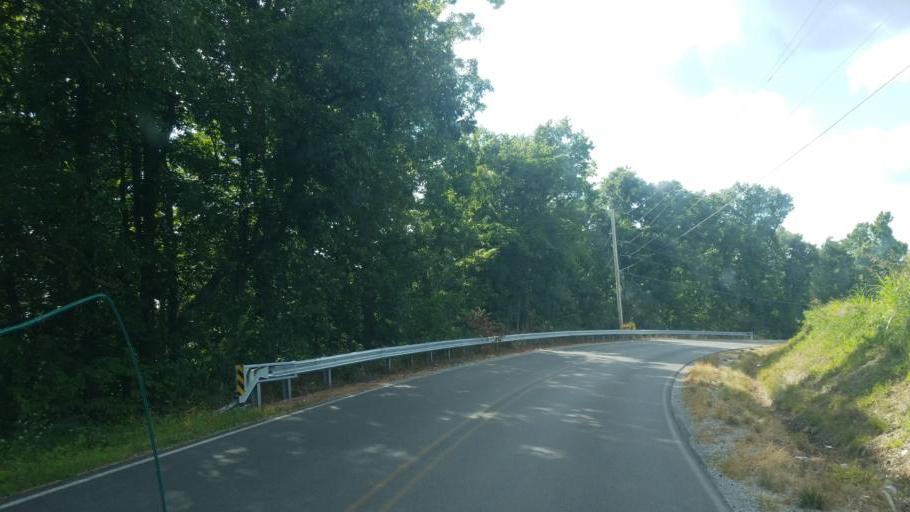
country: US
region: Illinois
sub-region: Union County
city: Cobden
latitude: 37.5624
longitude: -89.3084
